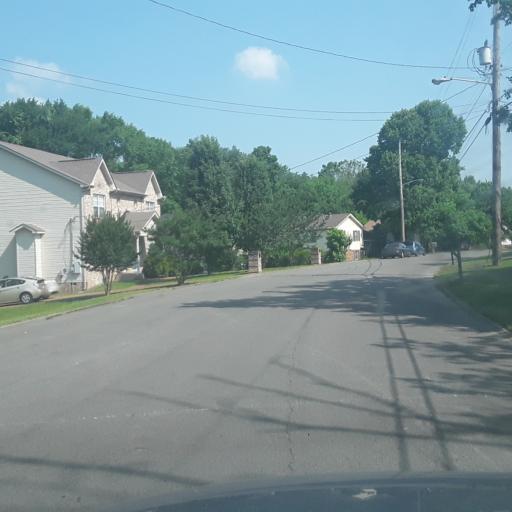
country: US
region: Tennessee
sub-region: Williamson County
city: Brentwood Estates
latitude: 36.0362
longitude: -86.7102
